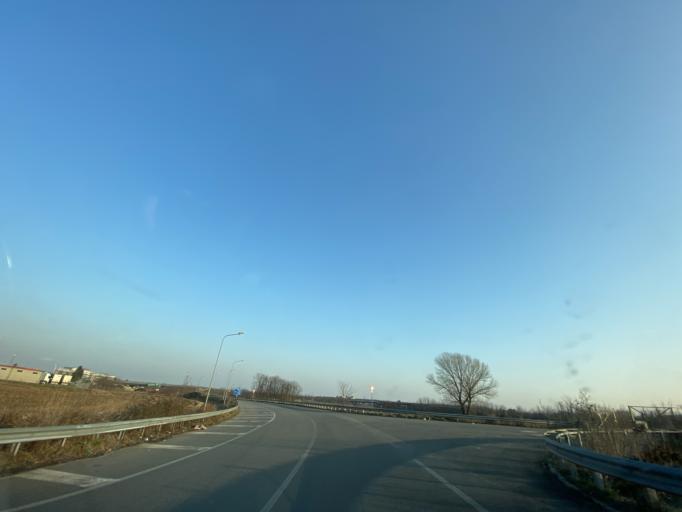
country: IT
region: Lombardy
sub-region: Citta metropolitana di Milano
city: Passirana
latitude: 45.5579
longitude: 9.0366
